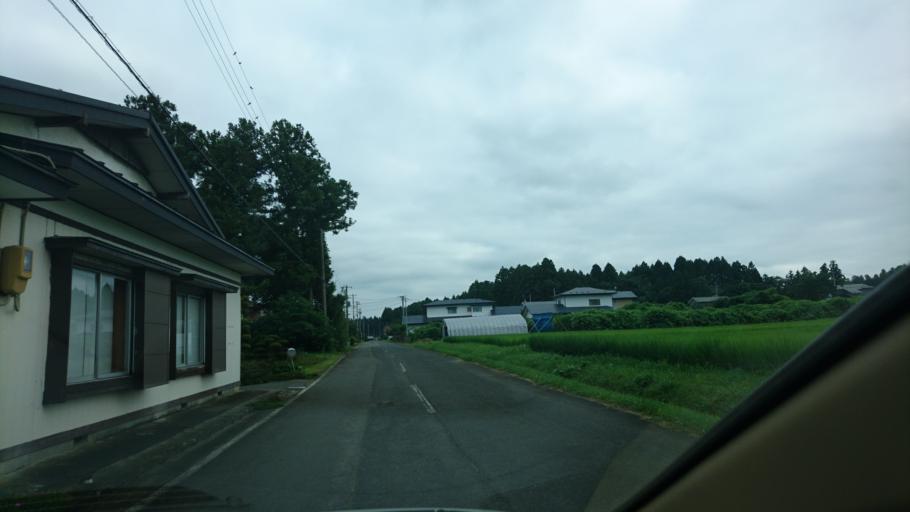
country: JP
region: Iwate
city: Kitakami
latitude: 39.2291
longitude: 141.1001
